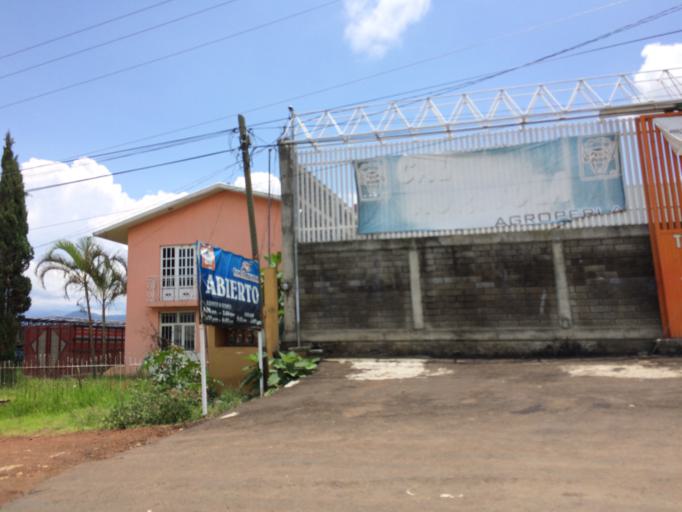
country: MX
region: Michoacan
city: Periban de Ramos
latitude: 19.5369
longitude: -102.4126
